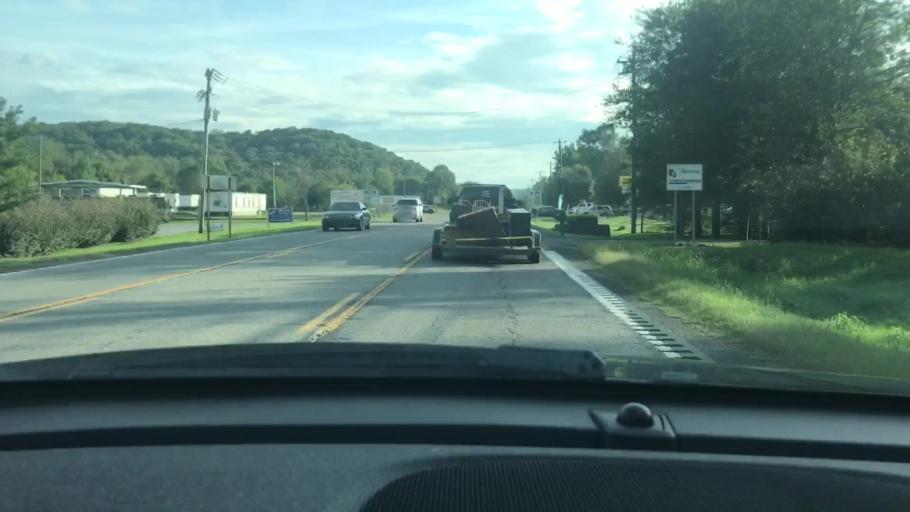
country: US
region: Tennessee
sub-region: Sumner County
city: Millersville
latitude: 36.3571
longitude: -86.7133
